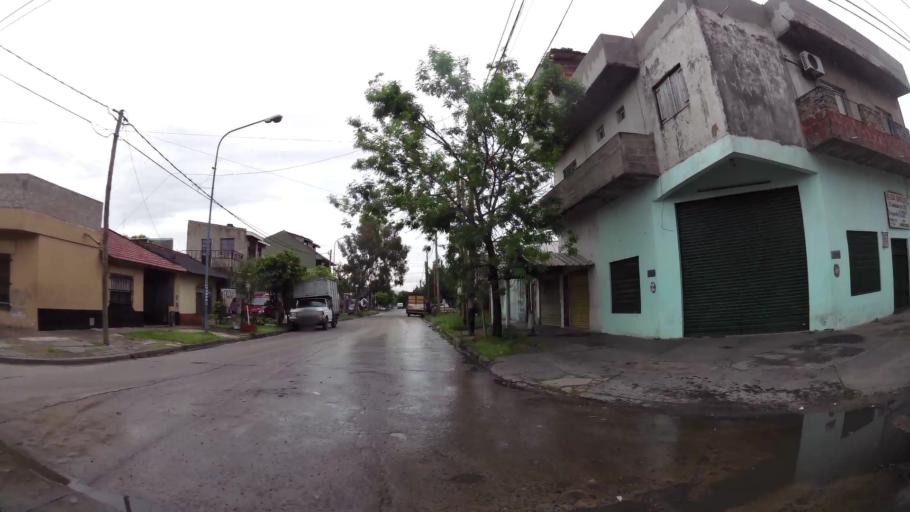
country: AR
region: Buenos Aires
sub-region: Partido de Lanus
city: Lanus
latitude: -34.7303
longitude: -58.3687
